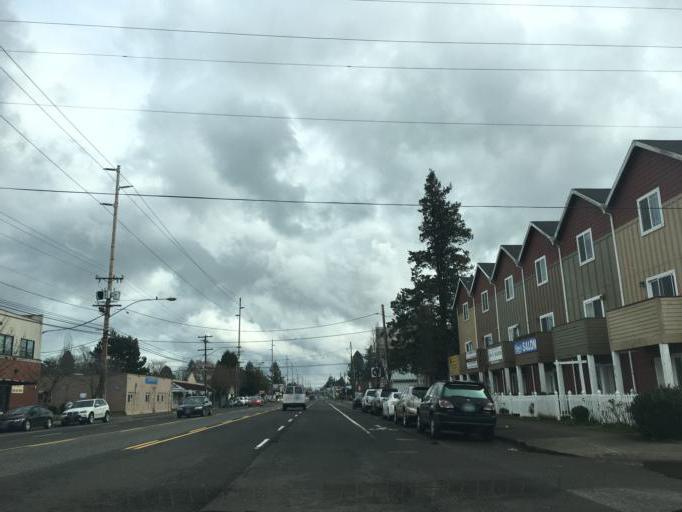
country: US
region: Oregon
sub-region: Multnomah County
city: Lents
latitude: 45.5045
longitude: -122.5734
